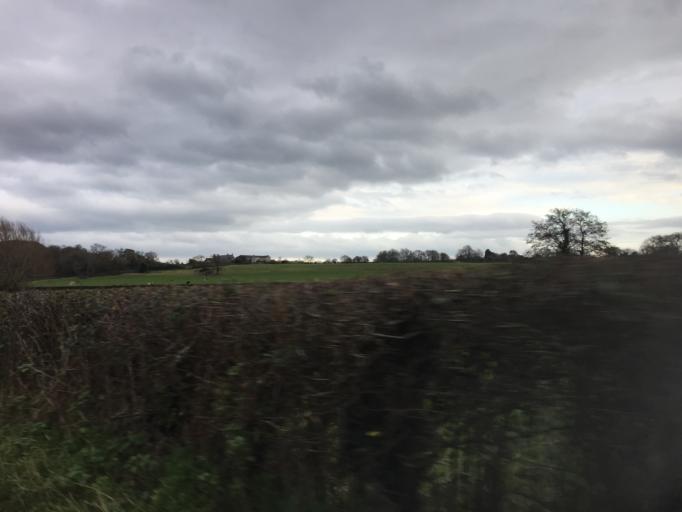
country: GB
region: Wales
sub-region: Monmouthshire
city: Magor
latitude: 51.5908
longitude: -2.8359
